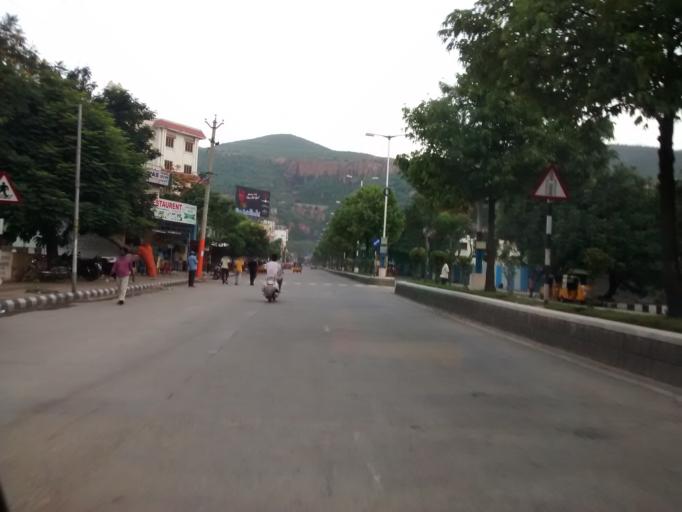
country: IN
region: Andhra Pradesh
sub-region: Chittoor
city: Akkarampalle
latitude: 13.6499
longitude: 79.4241
